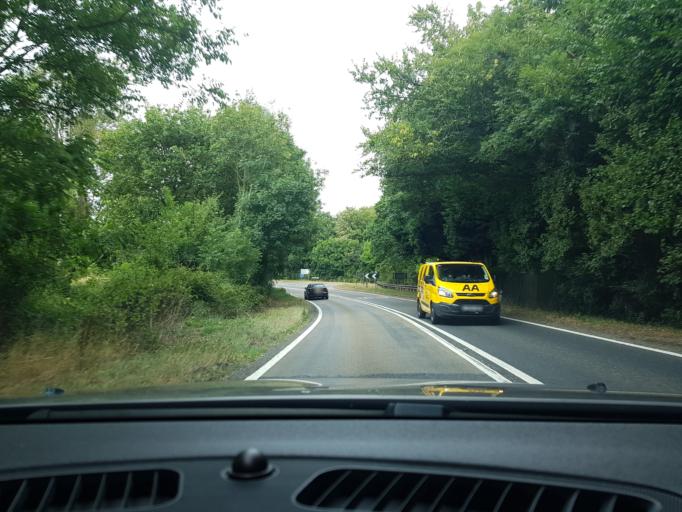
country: GB
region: England
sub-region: Hampshire
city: Kingsclere
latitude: 51.3192
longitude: -1.2101
